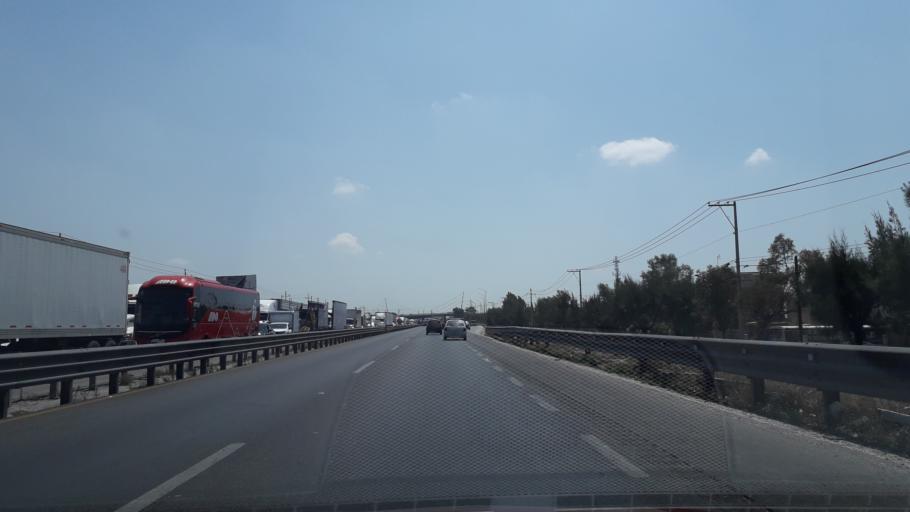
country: MX
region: Puebla
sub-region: Amozoc
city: Casa Blanca
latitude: 19.0682
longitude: -98.1238
